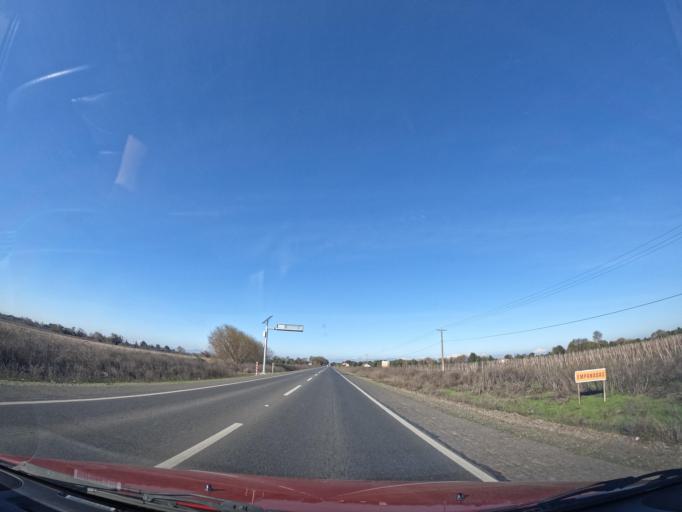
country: CL
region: Maule
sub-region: Provincia de Linares
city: San Javier
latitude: -35.6321
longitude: -71.7150
